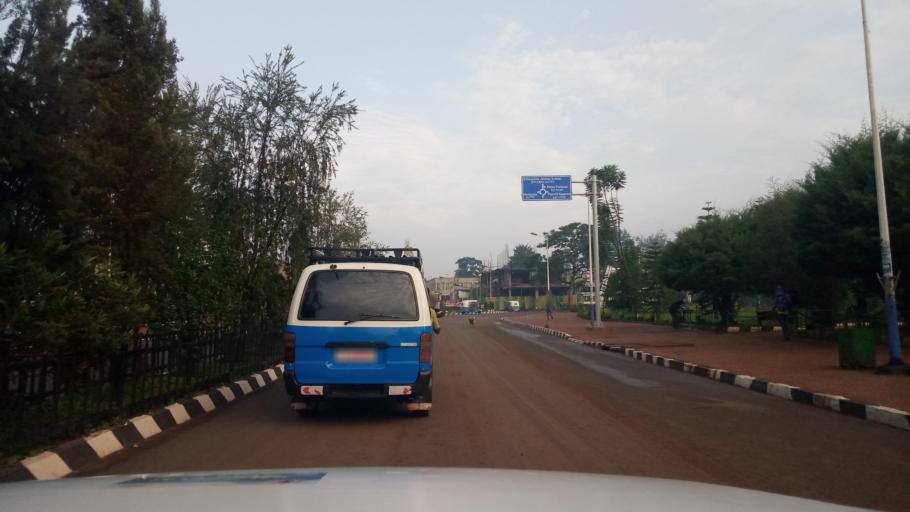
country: ET
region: Oromiya
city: Jima
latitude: 7.6761
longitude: 36.8353
